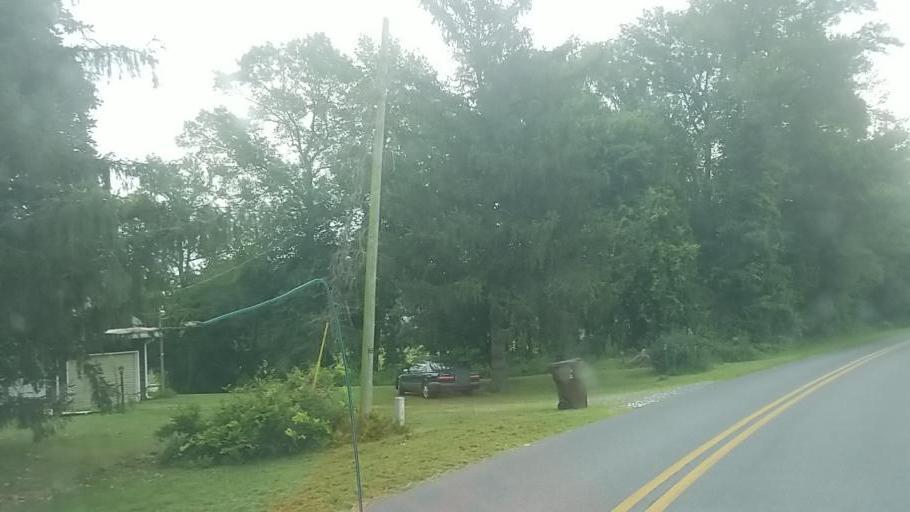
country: US
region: Delaware
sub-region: Sussex County
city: Selbyville
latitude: 38.4424
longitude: -75.1967
